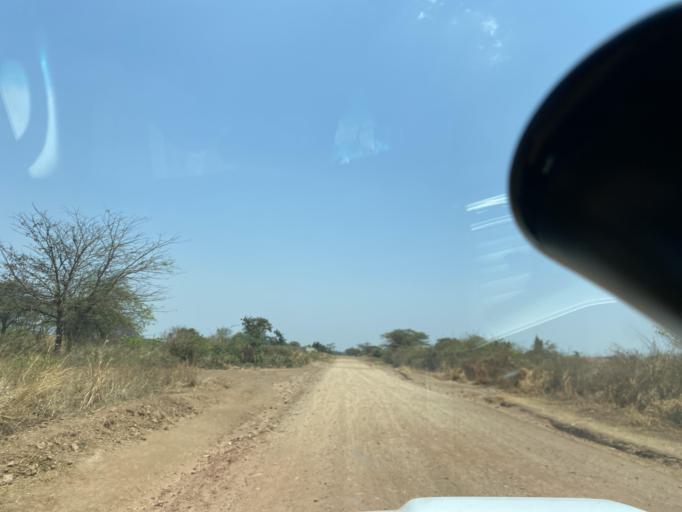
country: ZM
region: Lusaka
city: Lusaka
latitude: -15.4264
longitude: 28.0916
